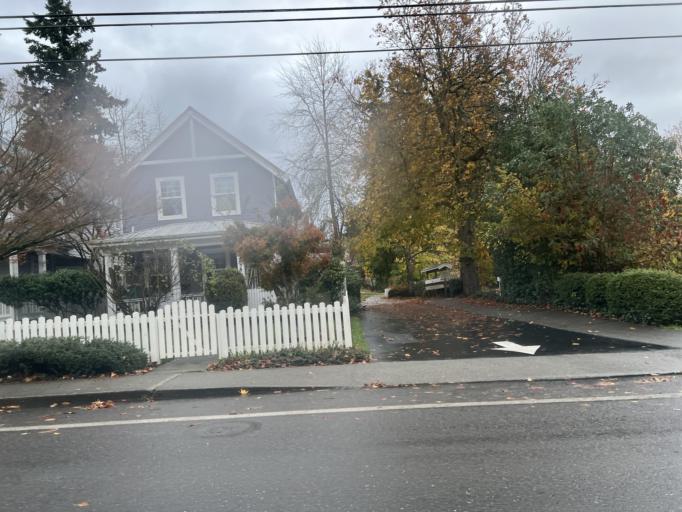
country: US
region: Washington
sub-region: Kitsap County
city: Bainbridge Island
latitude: 47.6298
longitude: -122.5210
